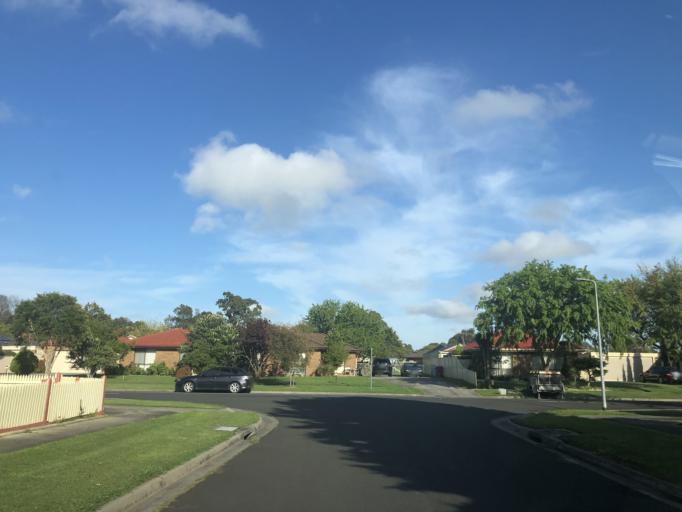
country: AU
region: Victoria
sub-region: Casey
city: Eumemmerring
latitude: -37.9969
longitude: 145.2606
